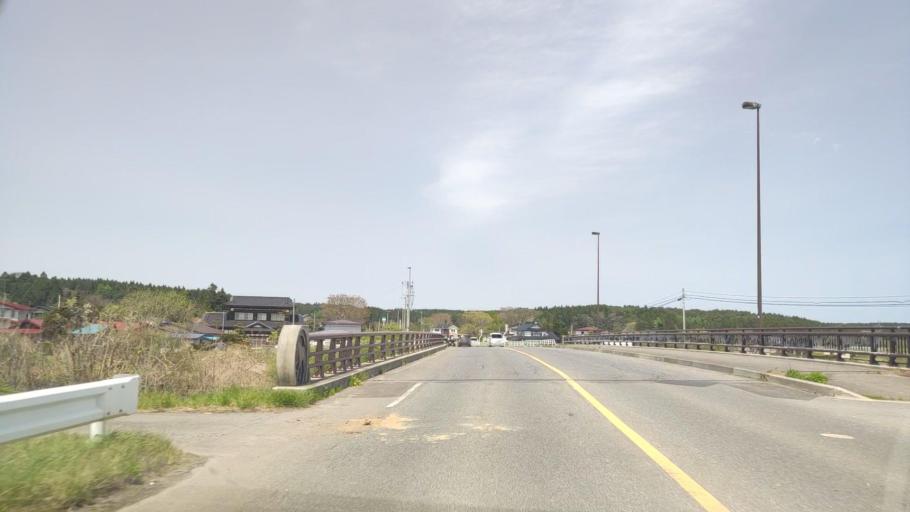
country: JP
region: Aomori
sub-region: Misawa Shi
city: Inuotose
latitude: 40.5564
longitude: 141.3884
